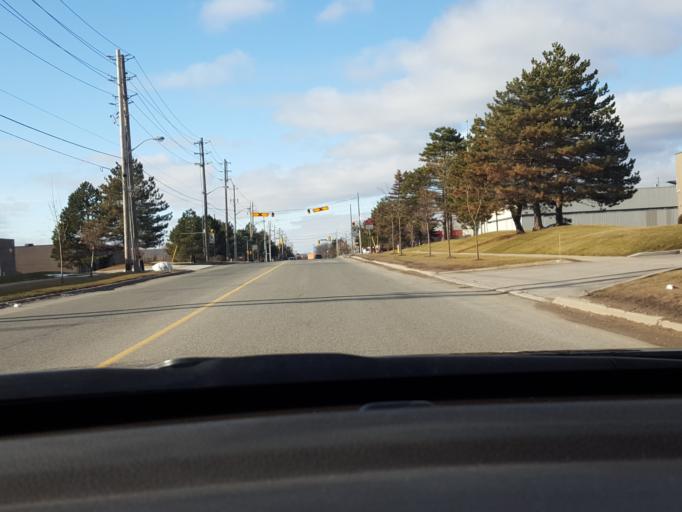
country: CA
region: Ontario
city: Concord
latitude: 43.7615
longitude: -79.5535
